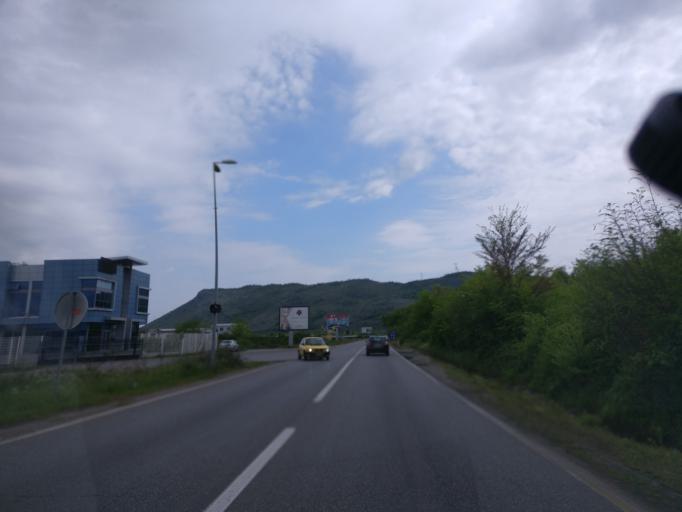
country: ME
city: Spuz
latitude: 42.4719
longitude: 19.1731
